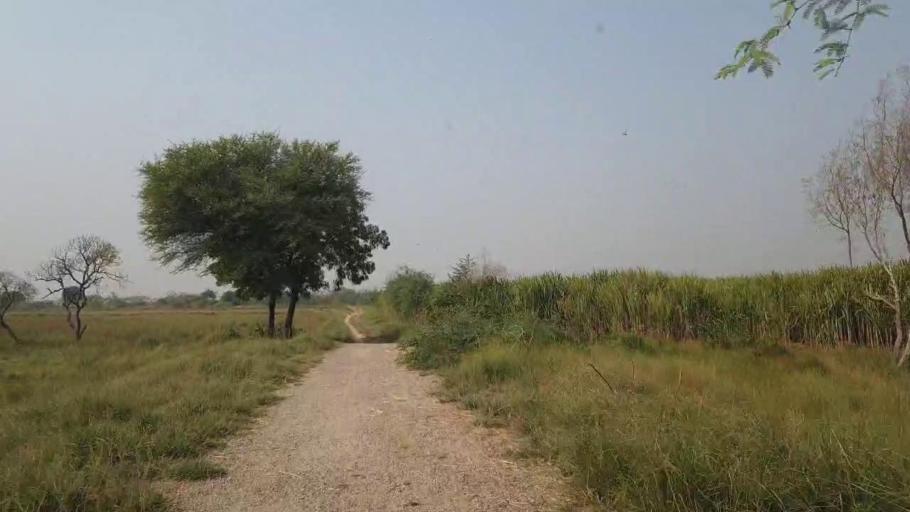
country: PK
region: Sindh
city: Matli
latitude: 25.1229
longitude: 68.6439
